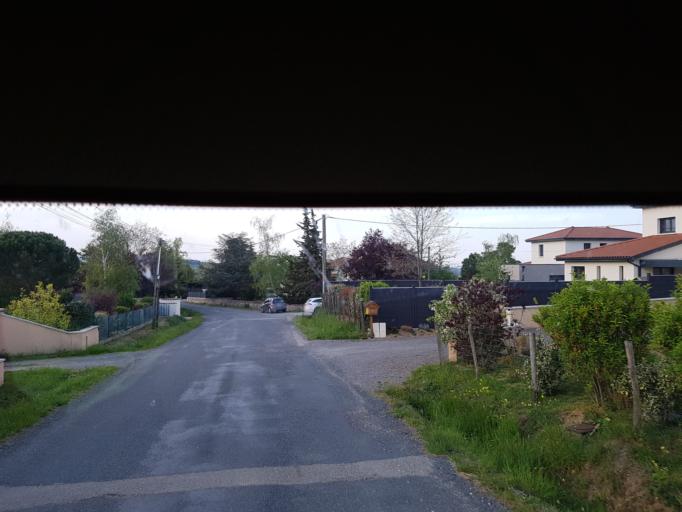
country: FR
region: Rhone-Alpes
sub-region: Departement du Rhone
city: Lentilly
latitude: 45.8084
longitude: 4.6532
